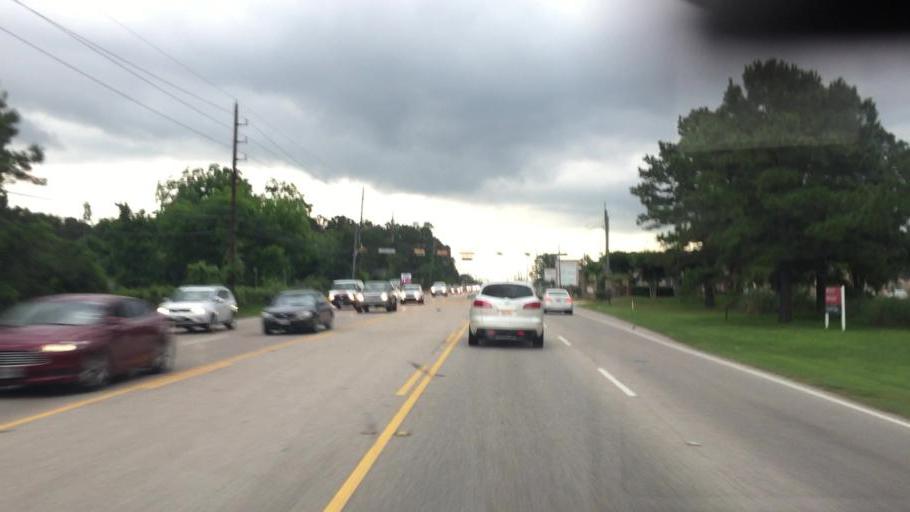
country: US
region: Texas
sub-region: Harris County
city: Spring
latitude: 30.0339
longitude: -95.5003
